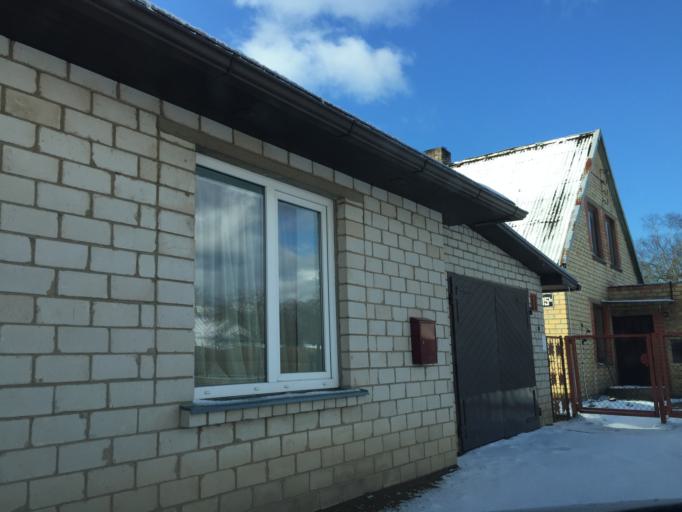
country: LV
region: Ventspils
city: Ventspils
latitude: 57.3813
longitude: 21.5651
